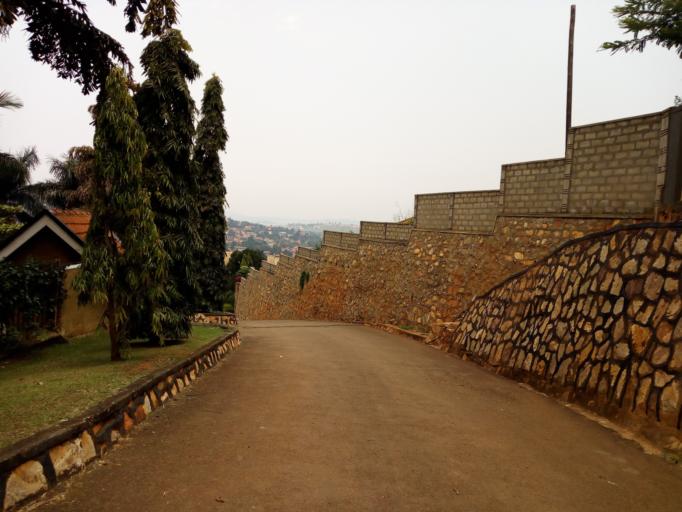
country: UG
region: Central Region
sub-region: Wakiso District
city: Kireka
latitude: 0.3261
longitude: 32.6334
